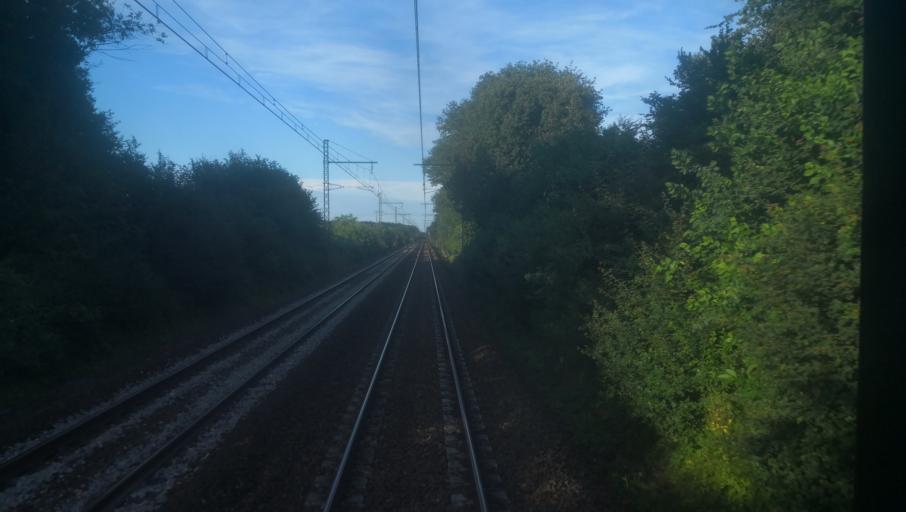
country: FR
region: Centre
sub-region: Departement de l'Indre
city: Deols
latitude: 46.8292
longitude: 1.7465
